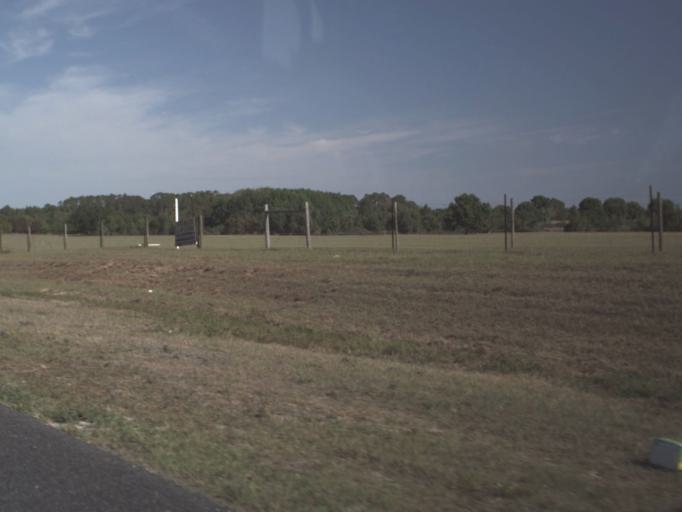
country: US
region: Florida
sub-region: Lake County
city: Mascotte
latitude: 28.6495
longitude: -81.8336
